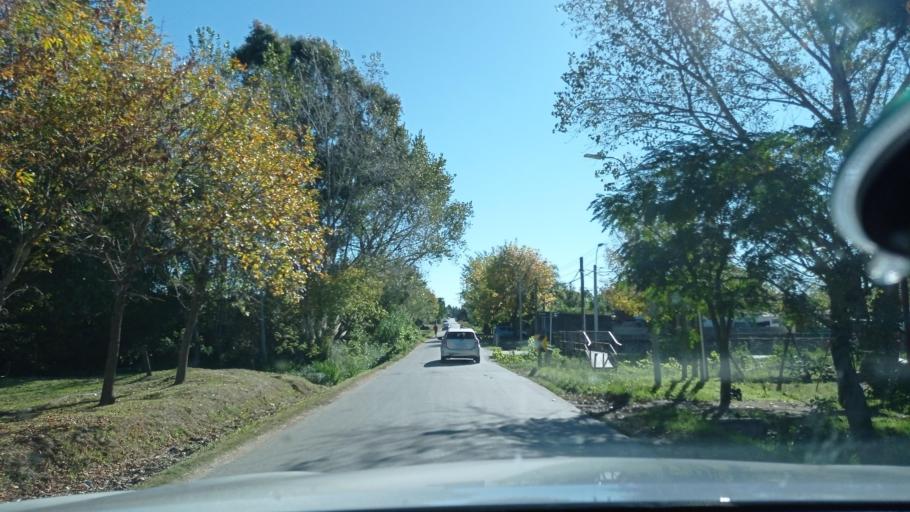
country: UY
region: Canelones
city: Joaquin Suarez
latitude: -34.7553
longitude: -55.9957
